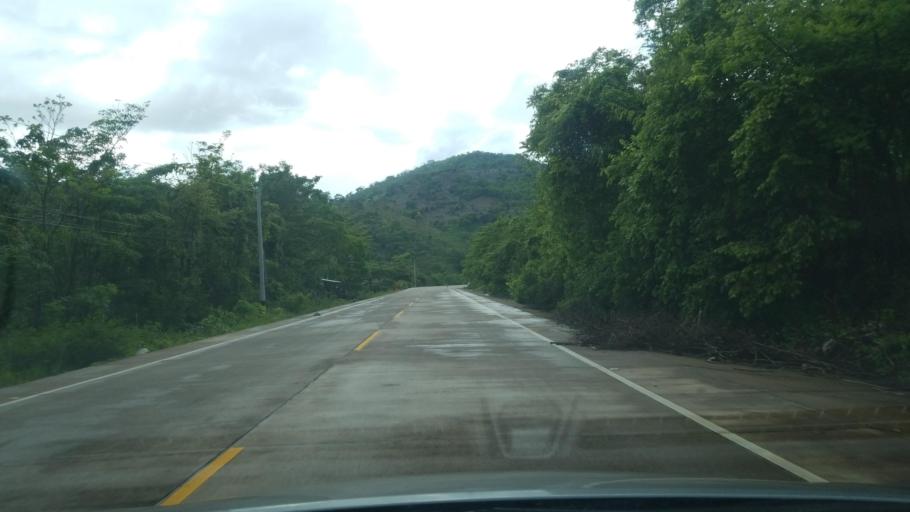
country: HN
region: Copan
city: Copan
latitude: 14.8483
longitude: -89.1949
